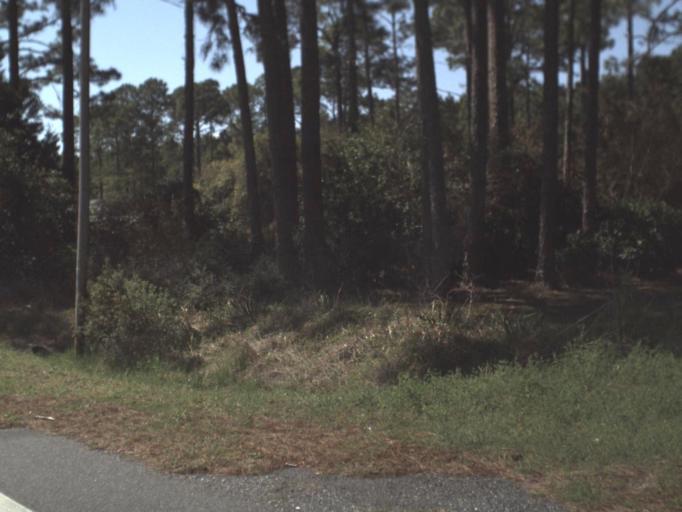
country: US
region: Florida
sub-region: Franklin County
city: Carrabelle
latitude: 29.9067
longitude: -84.5432
